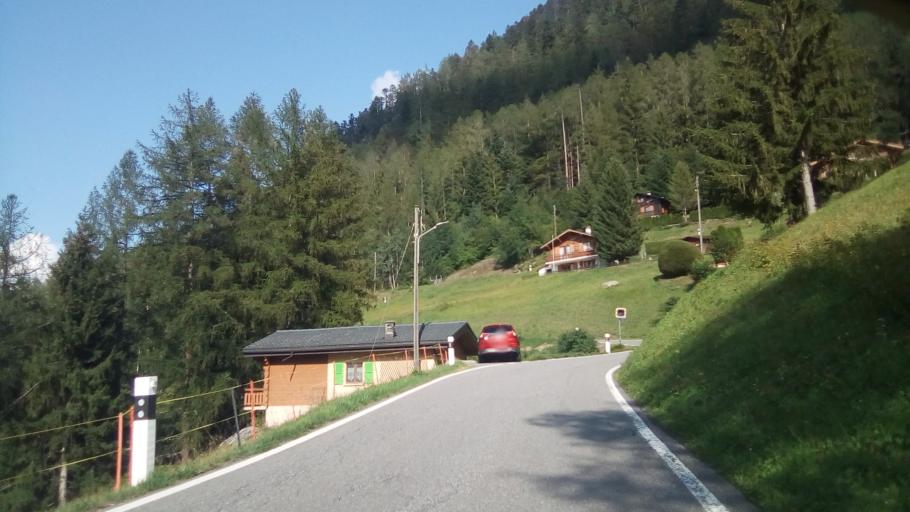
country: CH
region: Valais
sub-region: Martigny District
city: Martigny-Combe
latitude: 46.0651
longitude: 7.0764
